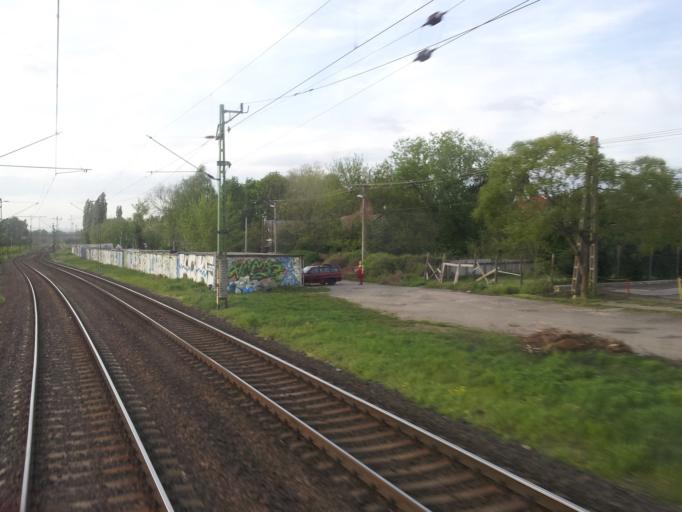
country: HU
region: Budapest
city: Budapest XVI. keruelet
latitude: 47.5150
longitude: 19.1514
